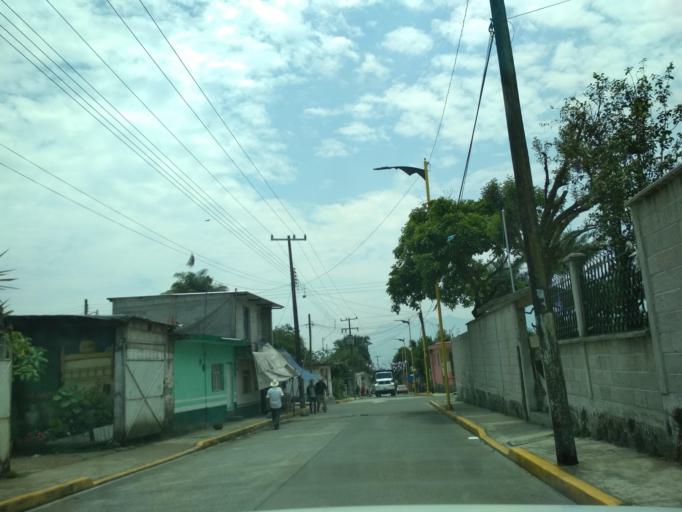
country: MX
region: Veracruz
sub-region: Mariano Escobedo
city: Mariano Escobedo
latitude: 18.9139
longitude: -97.1298
